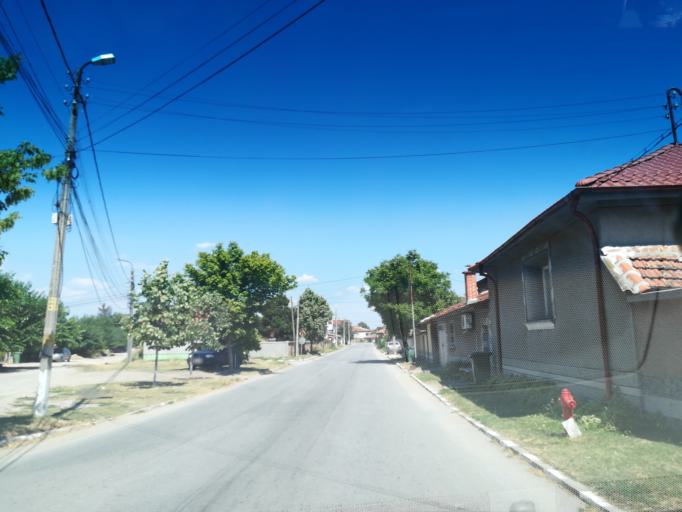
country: BG
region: Stara Zagora
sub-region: Obshtina Chirpan
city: Chirpan
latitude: 42.0753
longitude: 25.1889
